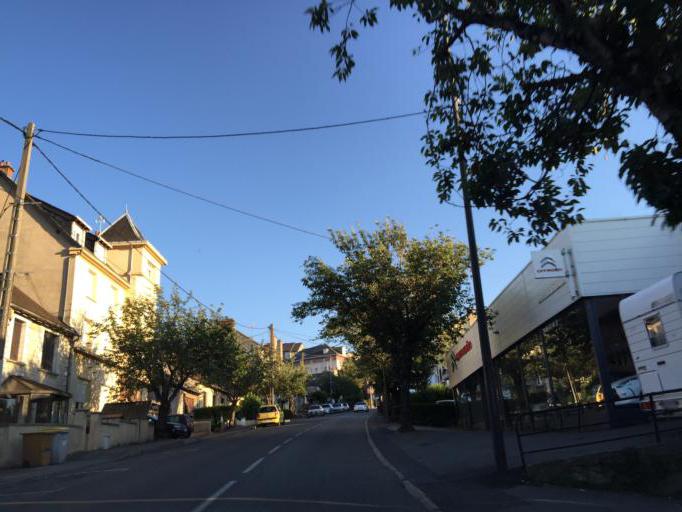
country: FR
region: Midi-Pyrenees
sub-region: Departement de l'Aveyron
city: Rodez
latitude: 44.3595
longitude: 2.5756
